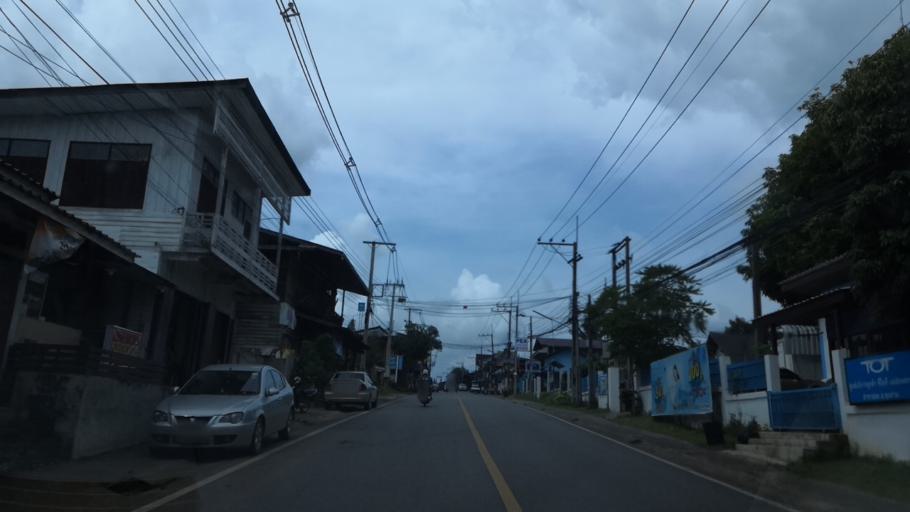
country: TH
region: Mae Hong Son
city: Khun Yuam
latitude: 18.8218
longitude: 97.9360
